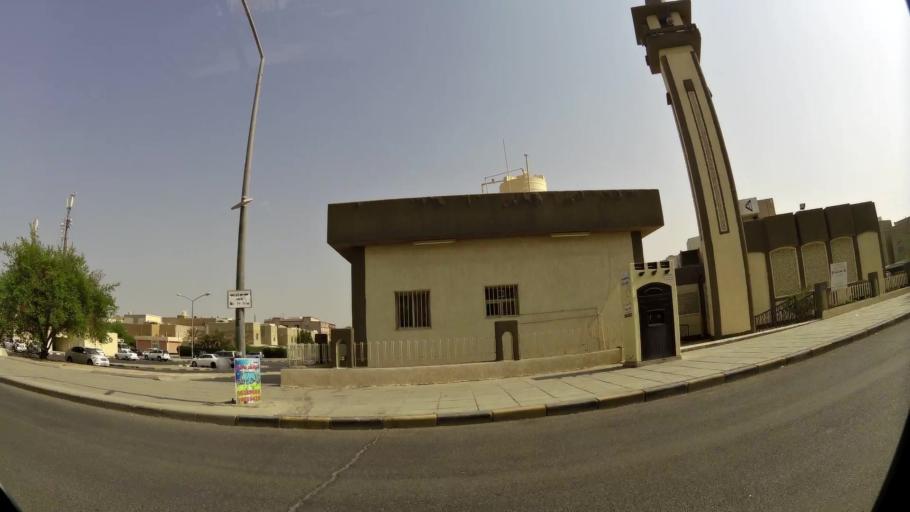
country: KW
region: Muhafazat al Jahra'
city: Al Jahra'
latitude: 29.3273
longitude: 47.6591
